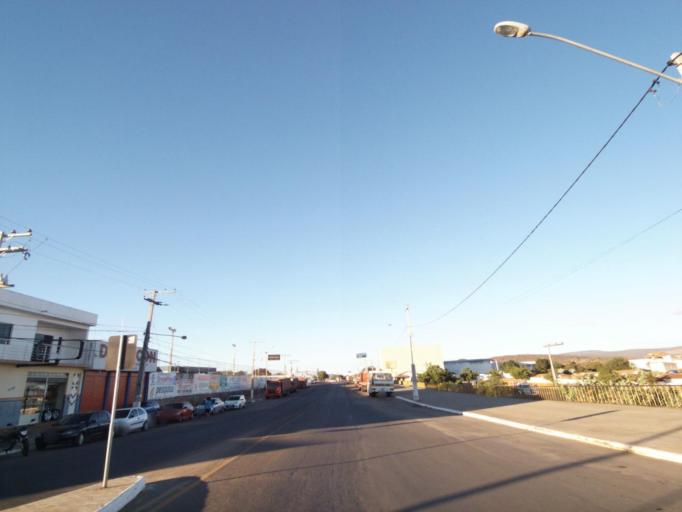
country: BR
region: Bahia
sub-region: Brumado
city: Brumado
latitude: -14.2155
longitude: -41.6805
